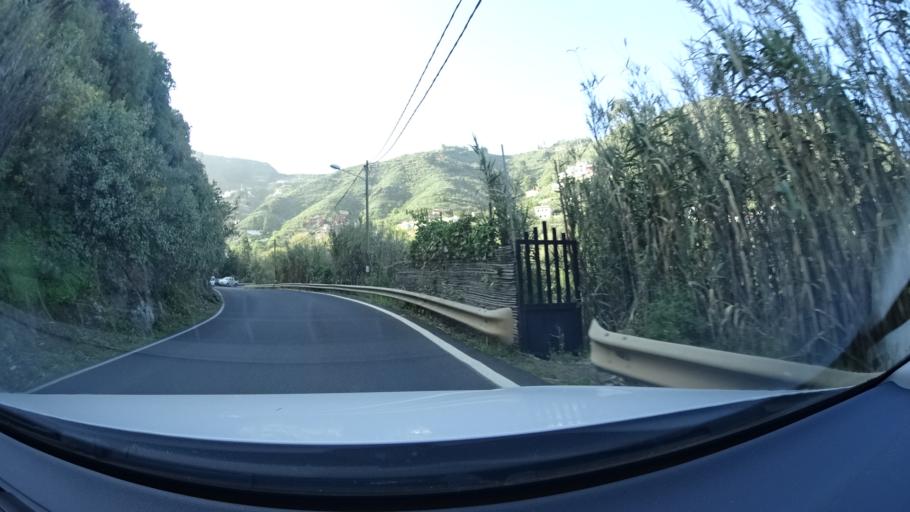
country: ES
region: Canary Islands
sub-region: Provincia de Las Palmas
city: Vega de San Mateo
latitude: 28.0171
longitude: -15.5549
